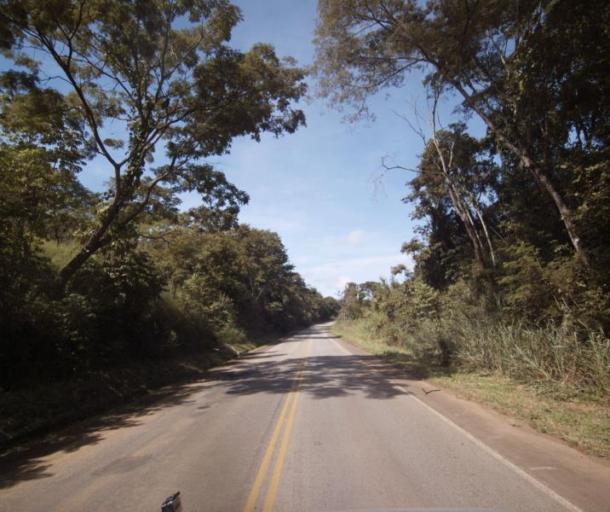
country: BR
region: Goias
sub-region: Abadiania
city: Abadiania
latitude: -16.1229
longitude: -48.8945
